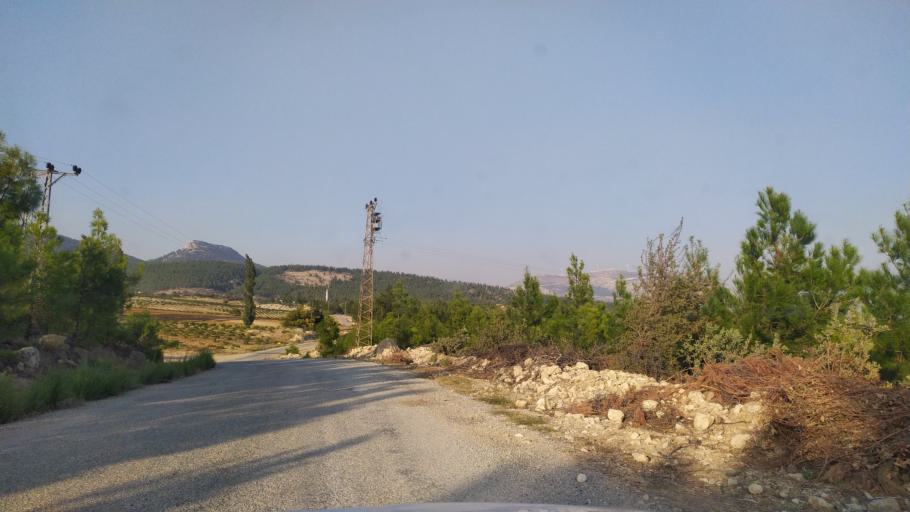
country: TR
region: Mersin
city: Mut
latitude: 36.6856
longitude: 33.1947
